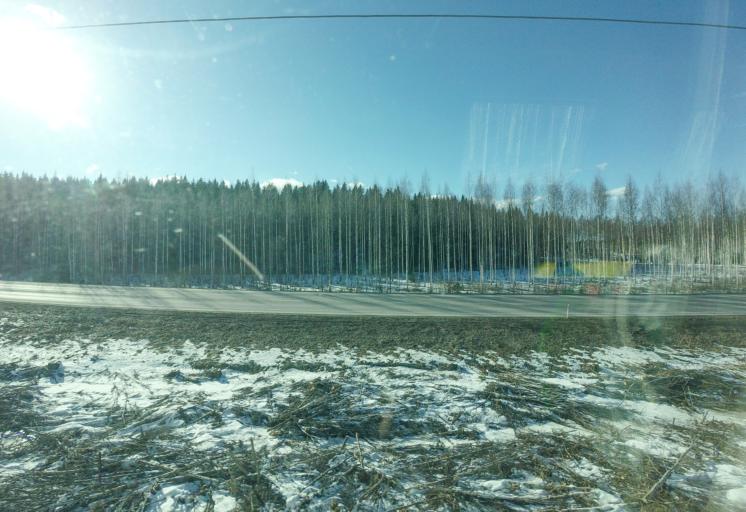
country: FI
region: South Karelia
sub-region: Imatra
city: Parikkala
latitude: 61.5221
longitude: 29.5144
